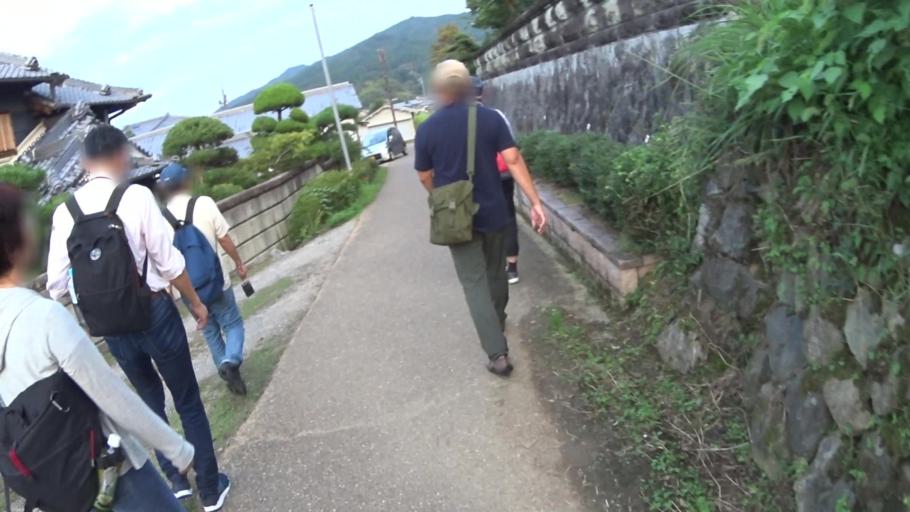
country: JP
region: Nara
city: Kashihara-shi
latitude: 34.4711
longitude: 135.8155
